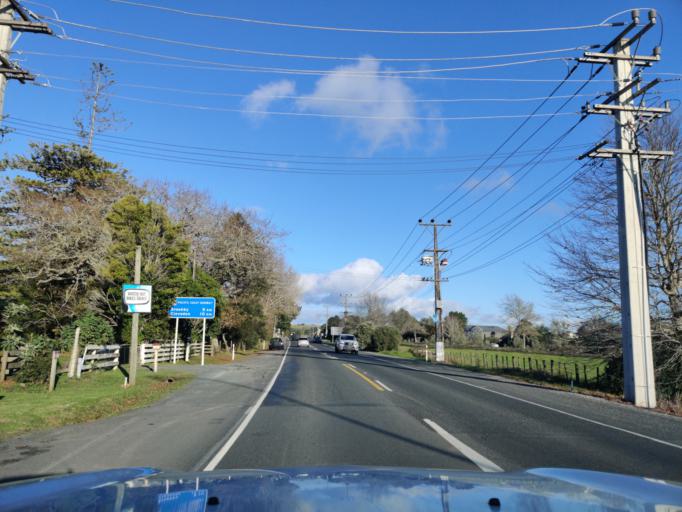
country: NZ
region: Auckland
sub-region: Auckland
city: Pakuranga
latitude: -36.9506
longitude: 174.9665
